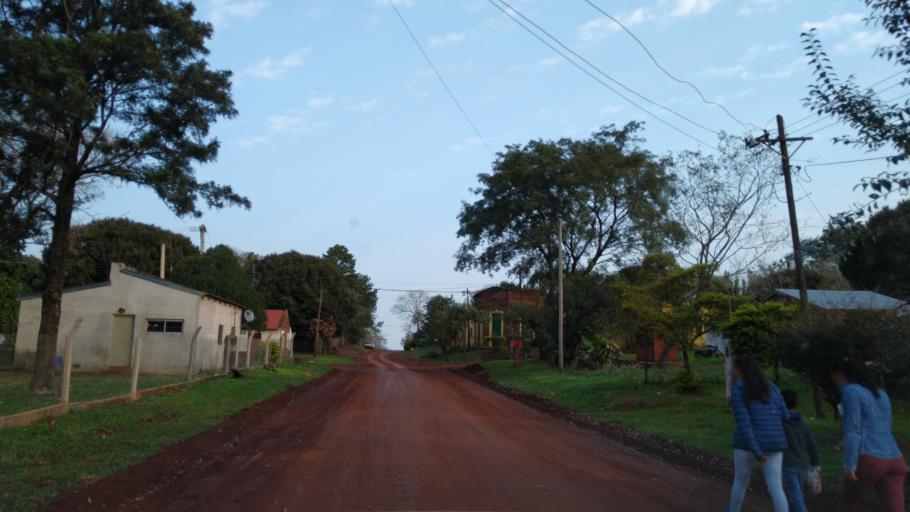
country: AR
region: Corrientes
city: San Carlos
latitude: -27.7471
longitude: -55.9010
